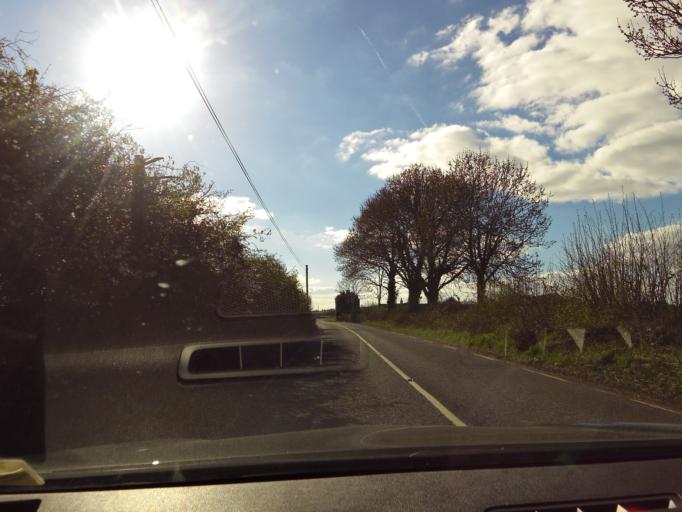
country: IE
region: Connaught
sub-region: County Galway
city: Portumna
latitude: 53.1103
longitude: -8.0941
